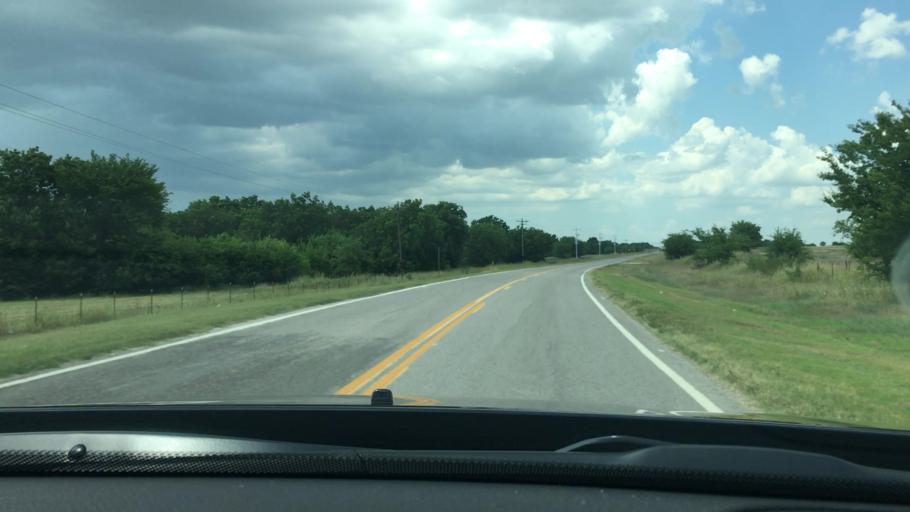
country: US
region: Oklahoma
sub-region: Pontotoc County
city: Ada
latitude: 34.5264
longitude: -96.6345
